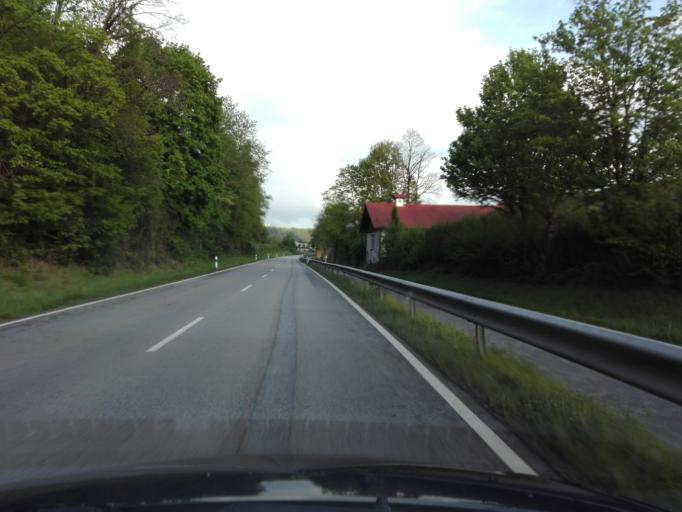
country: DE
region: Bavaria
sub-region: Lower Bavaria
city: Obernzell
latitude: 48.5622
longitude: 13.6158
